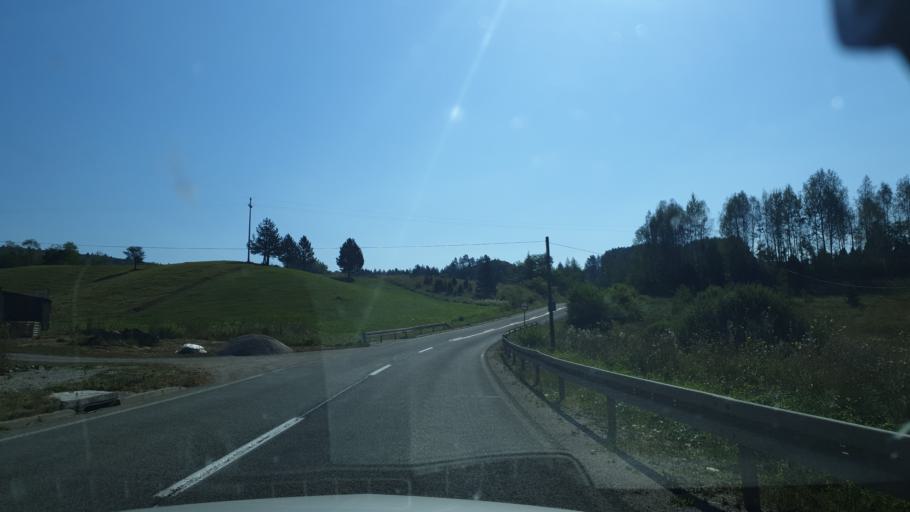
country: RS
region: Central Serbia
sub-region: Zlatiborski Okrug
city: Nova Varos
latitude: 43.5460
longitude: 19.7844
